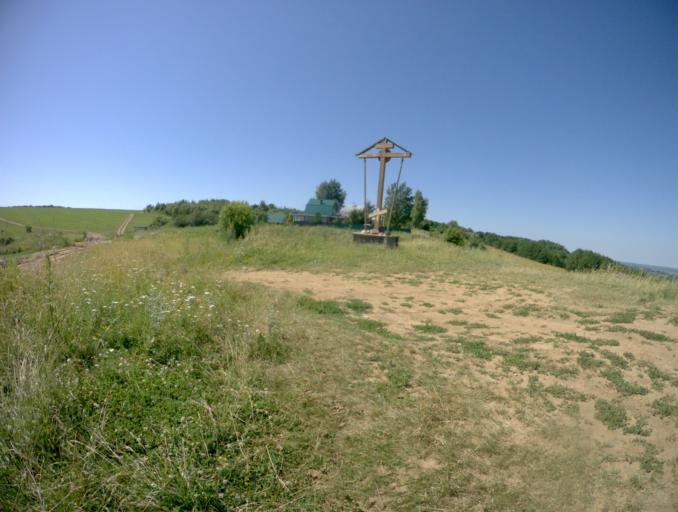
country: RU
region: Nizjnij Novgorod
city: Reshetikha
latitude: 56.1517
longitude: 43.3222
